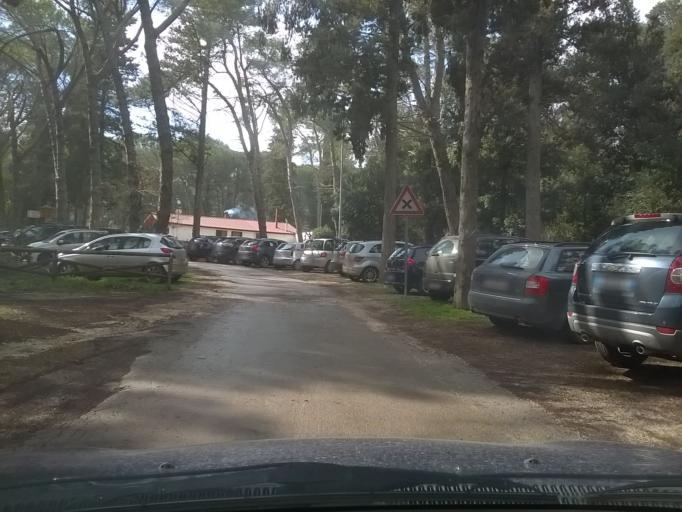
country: IT
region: Apulia
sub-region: Provincia di Bari
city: Cassano delle Murge
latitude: 40.8914
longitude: 16.6994
